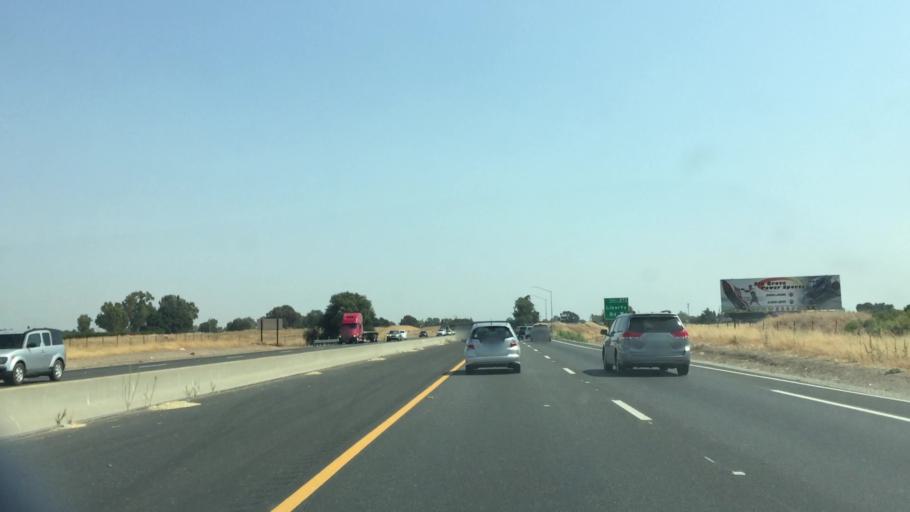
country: US
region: California
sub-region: Sacramento County
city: Galt
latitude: 38.2382
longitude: -121.2834
